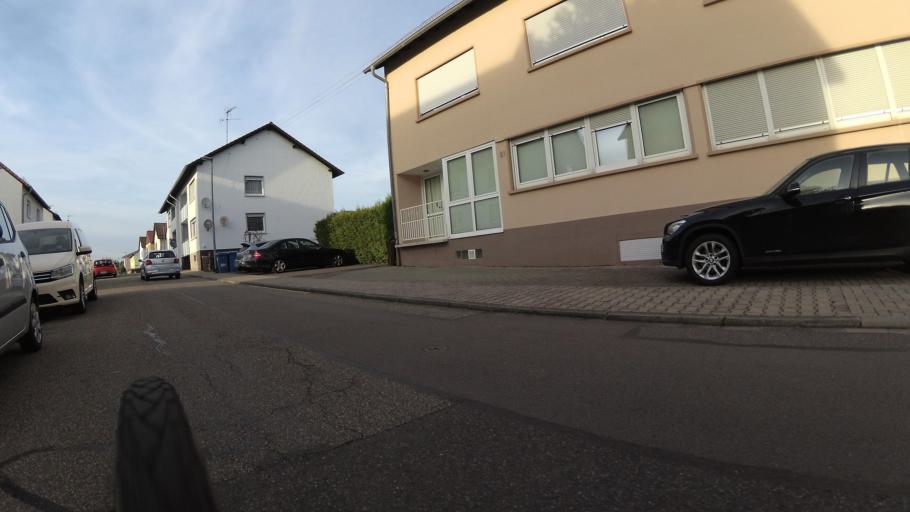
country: DE
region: Rheinland-Pfalz
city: Ramstein-Miesenbach
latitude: 49.4425
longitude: 7.5490
